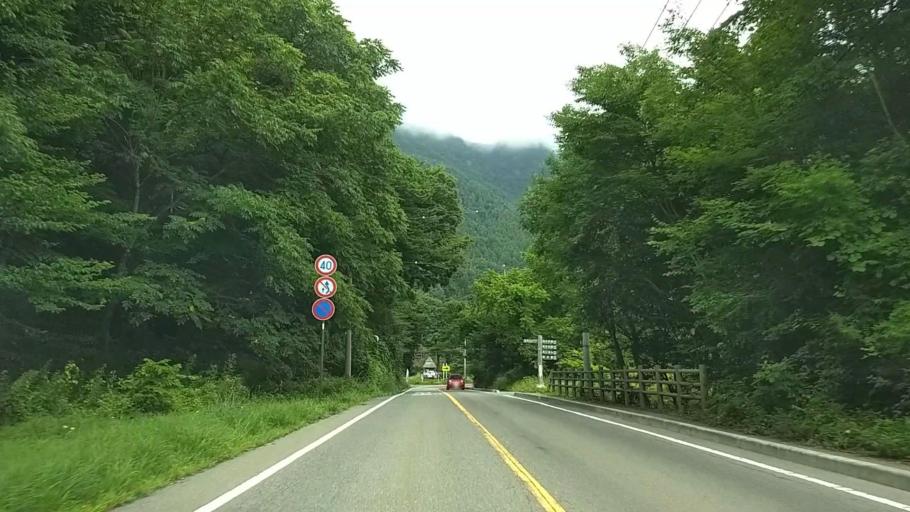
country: JP
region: Yamanashi
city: Fujikawaguchiko
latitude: 35.5004
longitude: 138.6590
